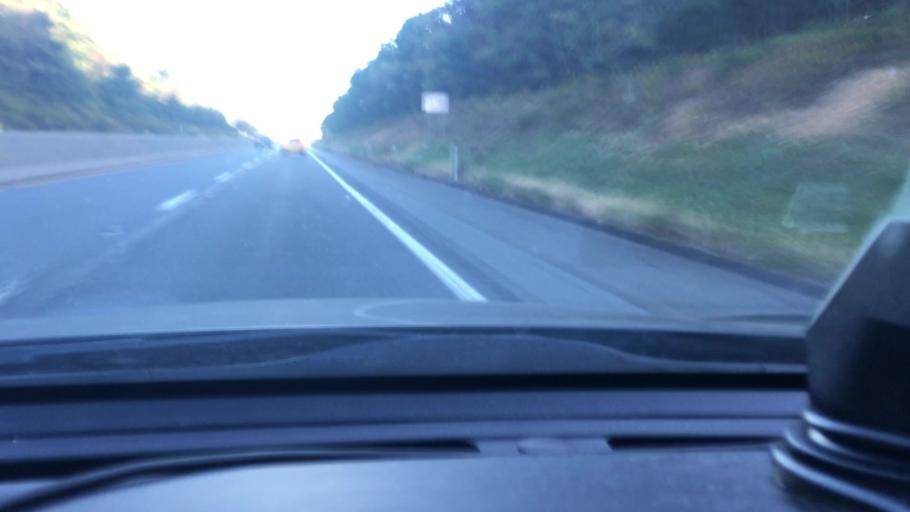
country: US
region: Pennsylvania
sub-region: Carbon County
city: Towamensing Trails
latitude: 40.9430
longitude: -75.6384
